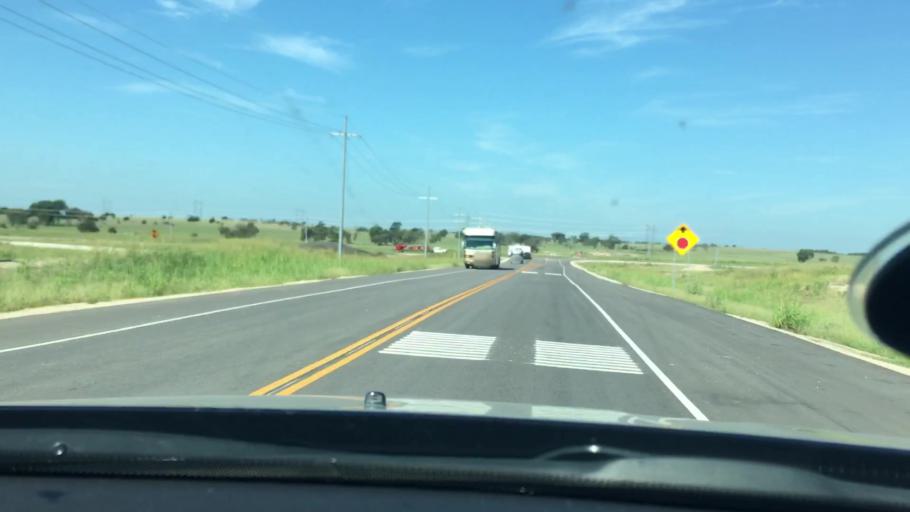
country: US
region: Oklahoma
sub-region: Johnston County
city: Tishomingo
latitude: 34.3612
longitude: -96.6328
